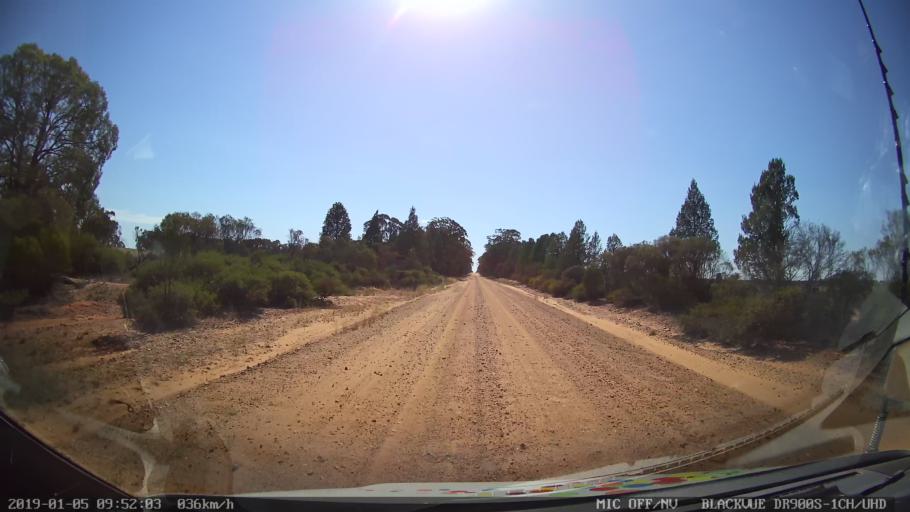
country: AU
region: New South Wales
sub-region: Gilgandra
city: Gilgandra
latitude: -31.6612
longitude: 148.7644
